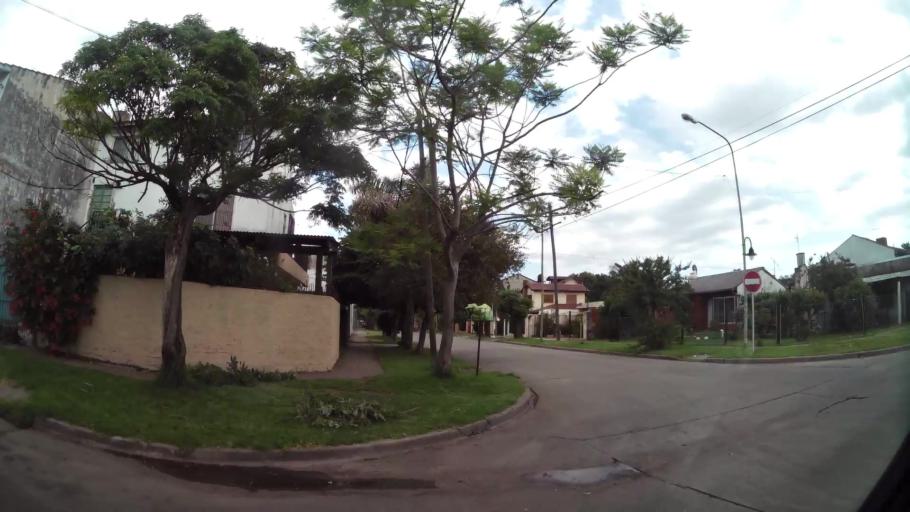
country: AR
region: Buenos Aires
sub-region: Partido de Tigre
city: Tigre
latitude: -34.4676
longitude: -58.6507
